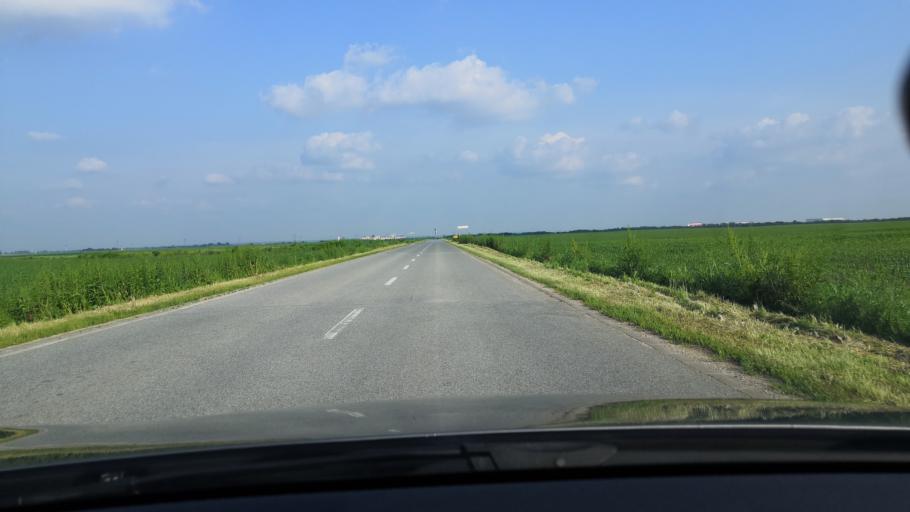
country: RS
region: Autonomna Pokrajina Vojvodina
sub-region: Sremski Okrug
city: Ingija
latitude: 45.0846
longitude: 20.1126
